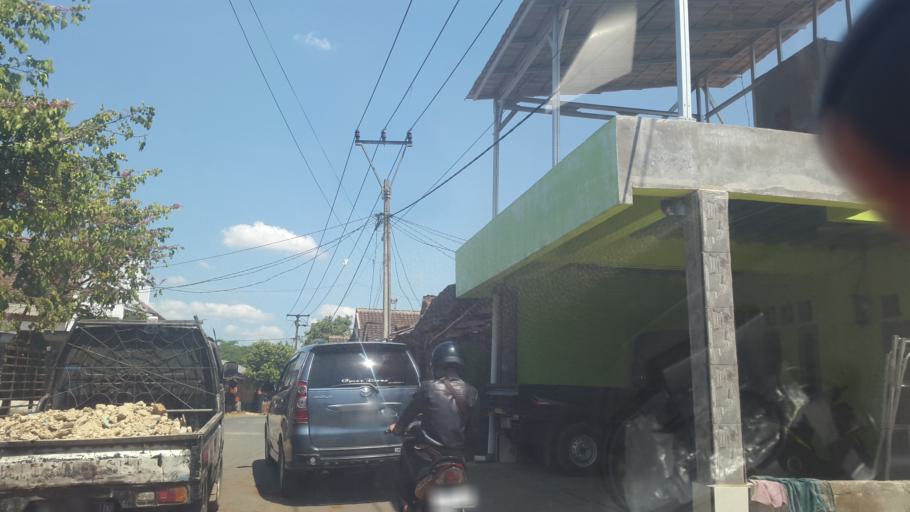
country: ID
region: West Java
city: Gunungkalong
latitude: -6.9761
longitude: 106.8244
